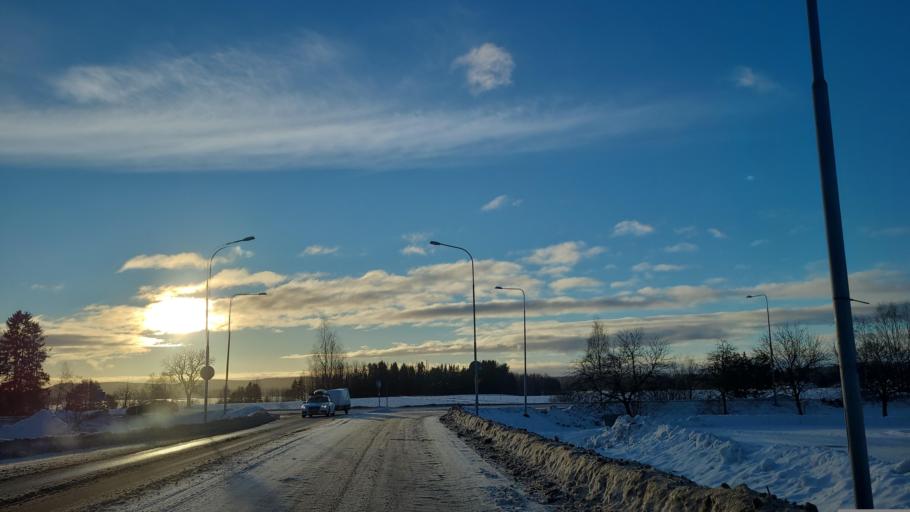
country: SE
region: Gaevleborg
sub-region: Bollnas Kommun
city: Bollnas
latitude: 61.3563
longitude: 16.4236
